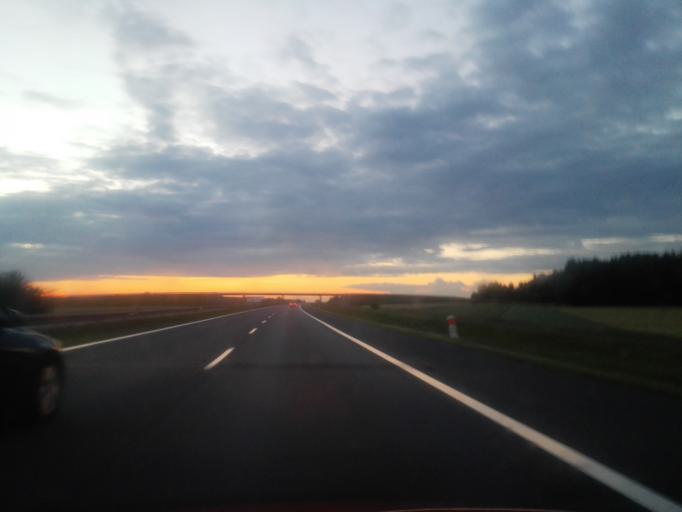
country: PL
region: Lodz Voivodeship
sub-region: Powiat piotrkowski
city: Grabica
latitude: 51.4955
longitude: 19.6103
